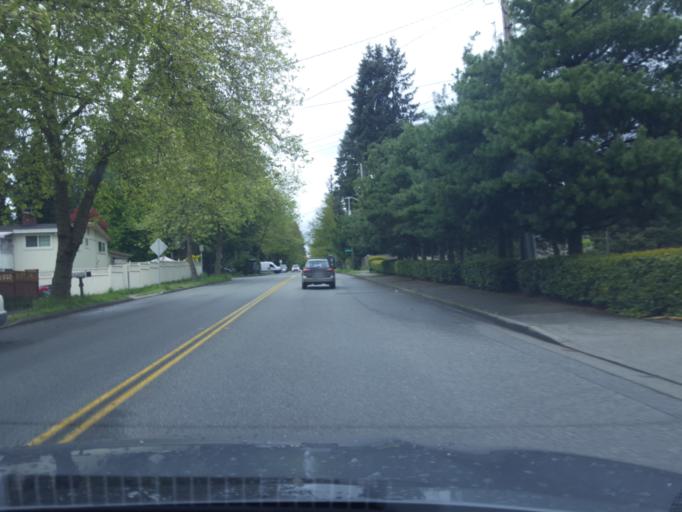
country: US
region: Washington
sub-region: King County
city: Shoreline
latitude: 47.7606
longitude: -122.3349
